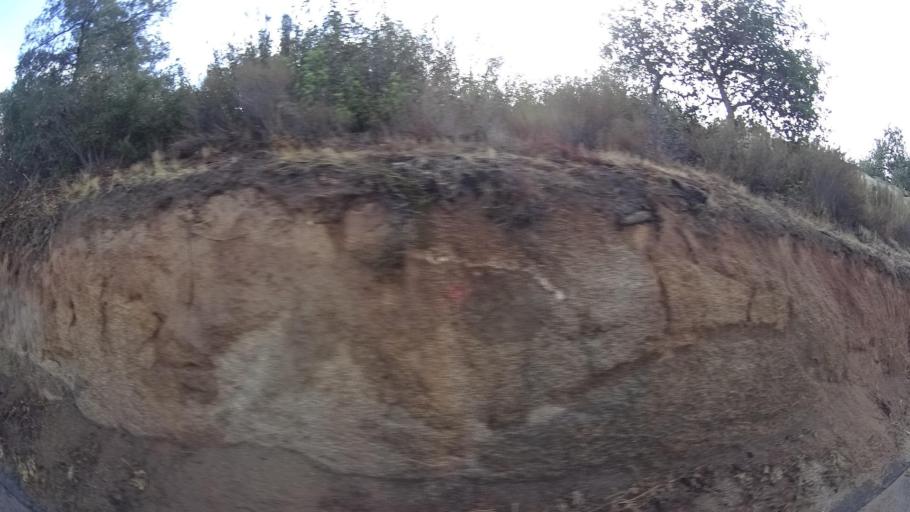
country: MX
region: Baja California
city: Tecate
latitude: 32.6448
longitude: -116.6358
